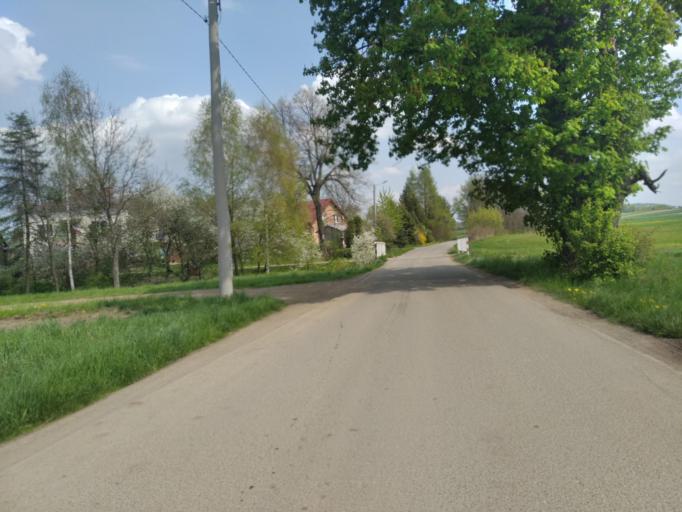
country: PL
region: Subcarpathian Voivodeship
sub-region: Powiat brzozowski
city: Jasionow
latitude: 49.6446
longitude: 21.9832
